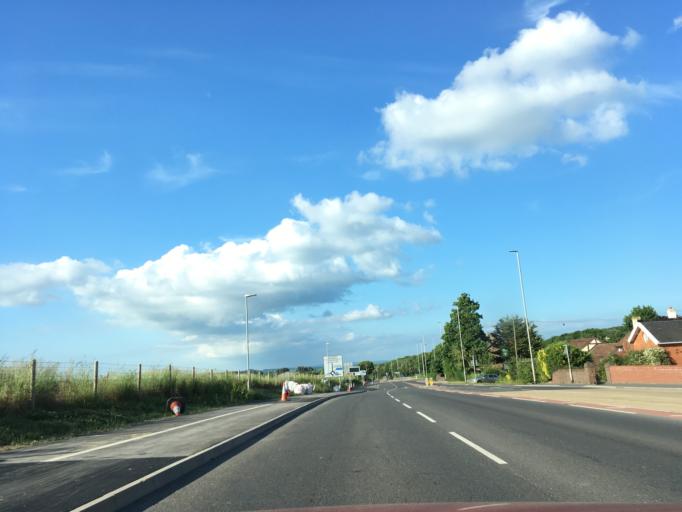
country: GB
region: England
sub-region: Somerset
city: North Petherton
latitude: 51.1021
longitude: -3.0008
